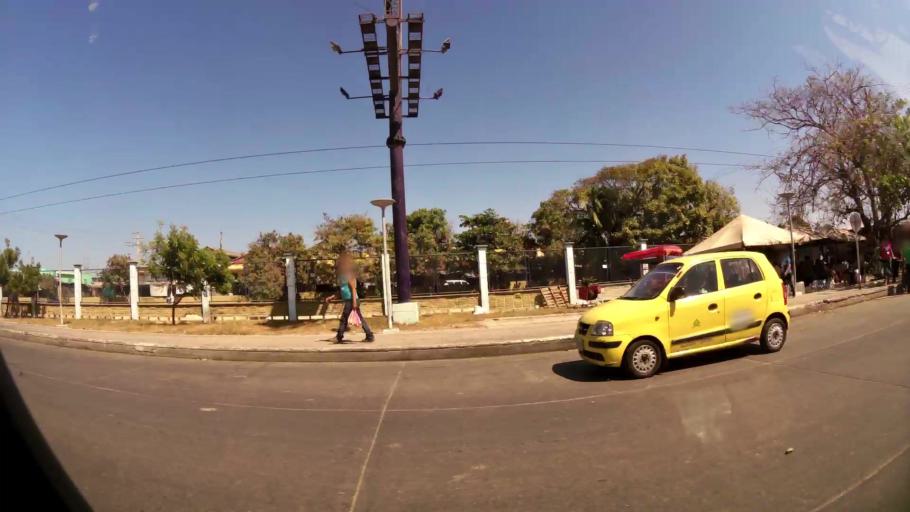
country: CO
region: Atlantico
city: Barranquilla
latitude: 10.9817
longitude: -74.7753
